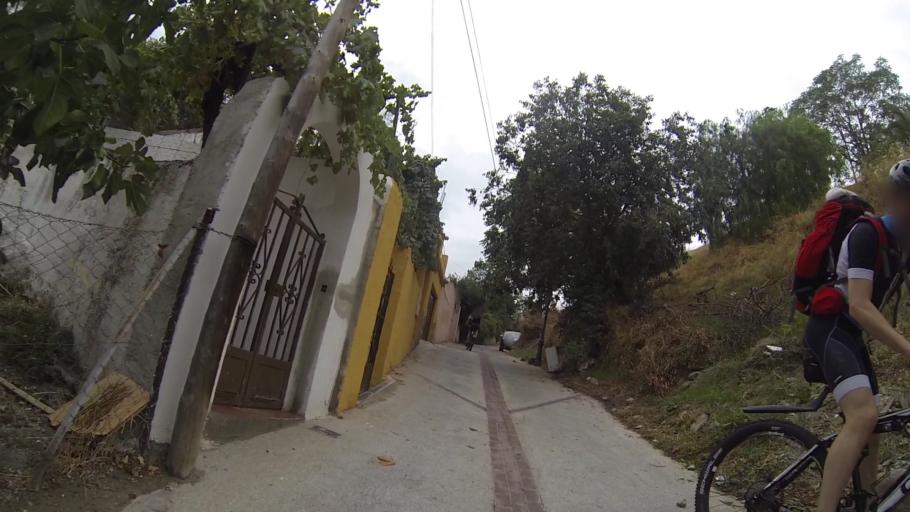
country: ES
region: Andalusia
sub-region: Provincia de Granada
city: Huetor Vega
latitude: 37.1707
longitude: -3.5841
